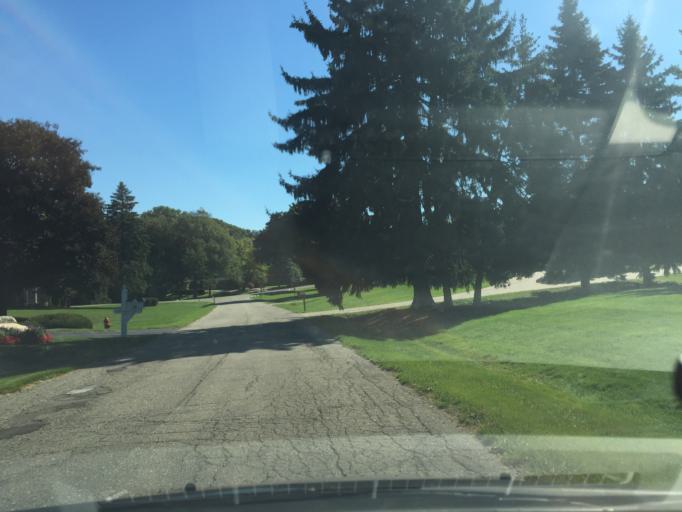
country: US
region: Michigan
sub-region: Oakland County
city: Franklin
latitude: 42.5695
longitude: -83.2985
